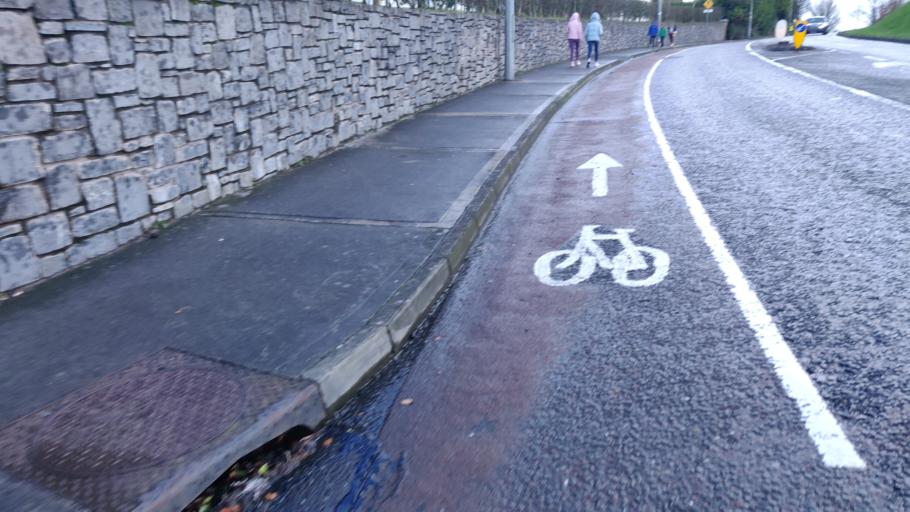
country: IE
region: Munster
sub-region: County Cork
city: Cork
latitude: 51.8719
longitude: -8.4201
